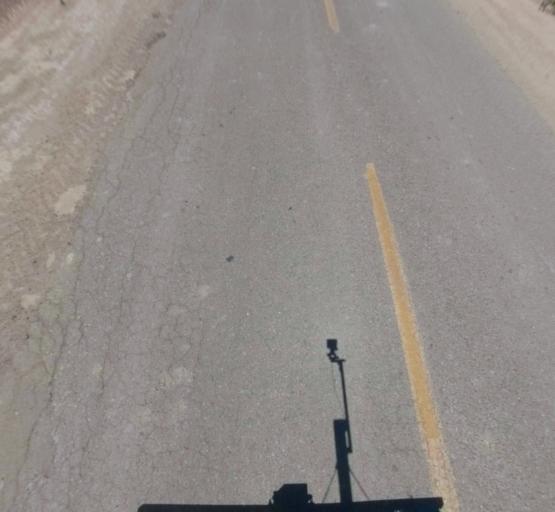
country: US
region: California
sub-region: Merced County
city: Dos Palos
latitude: 37.0546
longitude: -120.4635
